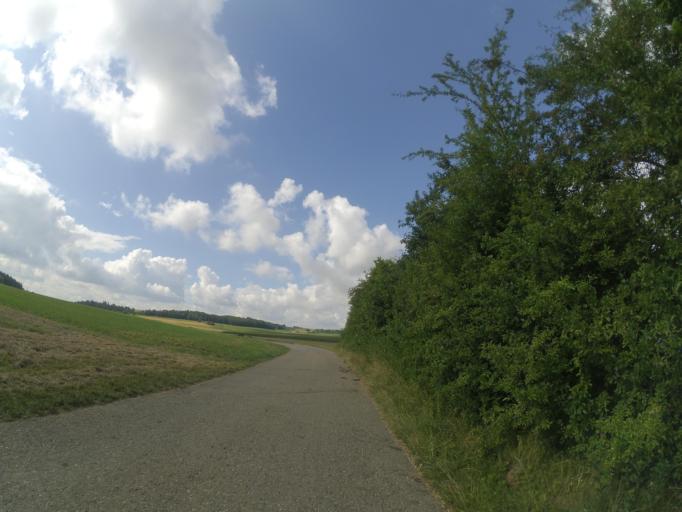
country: DE
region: Baden-Wuerttemberg
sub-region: Tuebingen Region
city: Bernstadt
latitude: 48.4952
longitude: 10.0169
